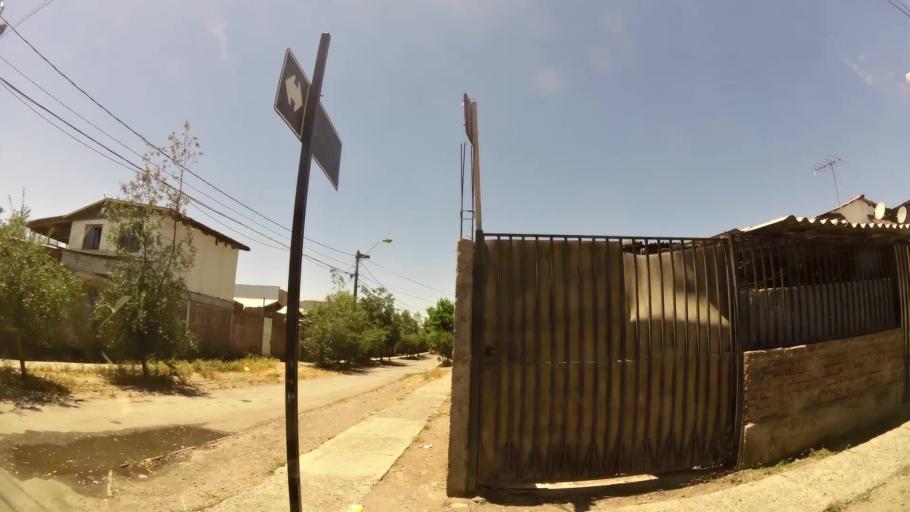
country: CL
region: Santiago Metropolitan
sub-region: Provincia de Maipo
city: San Bernardo
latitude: -33.5750
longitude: -70.6711
